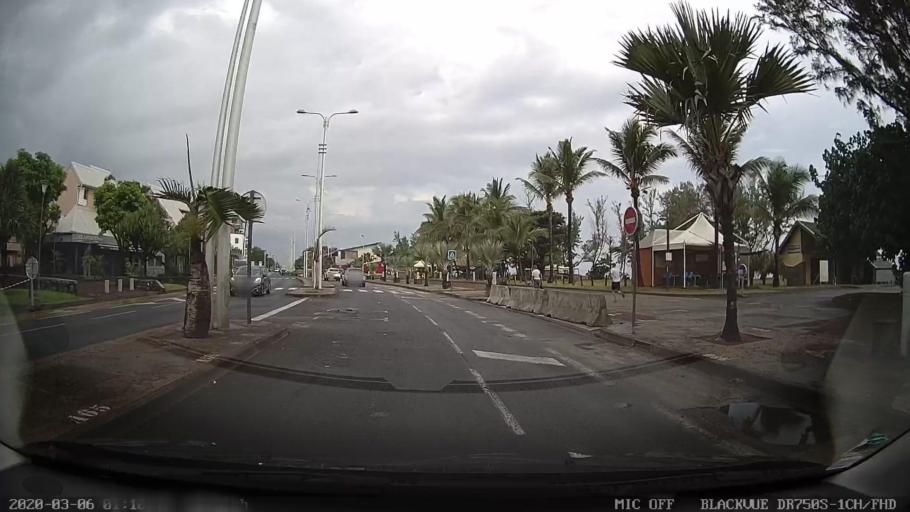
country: RE
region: Reunion
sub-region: Reunion
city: Saint-Pierre
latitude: -21.3412
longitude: 55.4596
